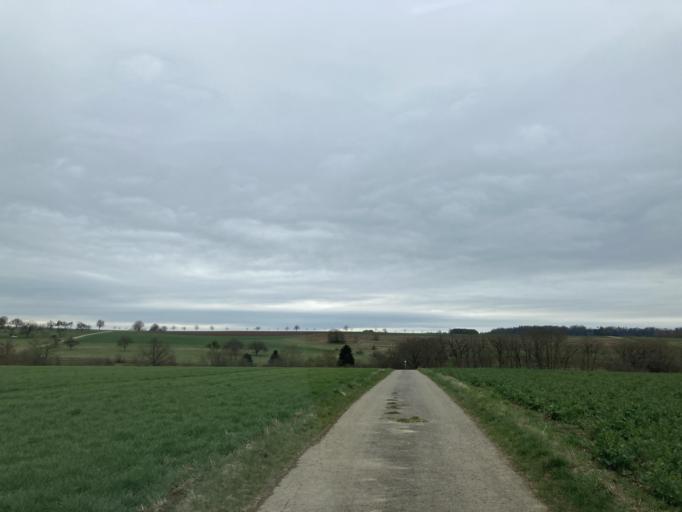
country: DE
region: Baden-Wuerttemberg
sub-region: Regierungsbezirk Stuttgart
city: Herrenberg
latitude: 48.5412
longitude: 8.8944
